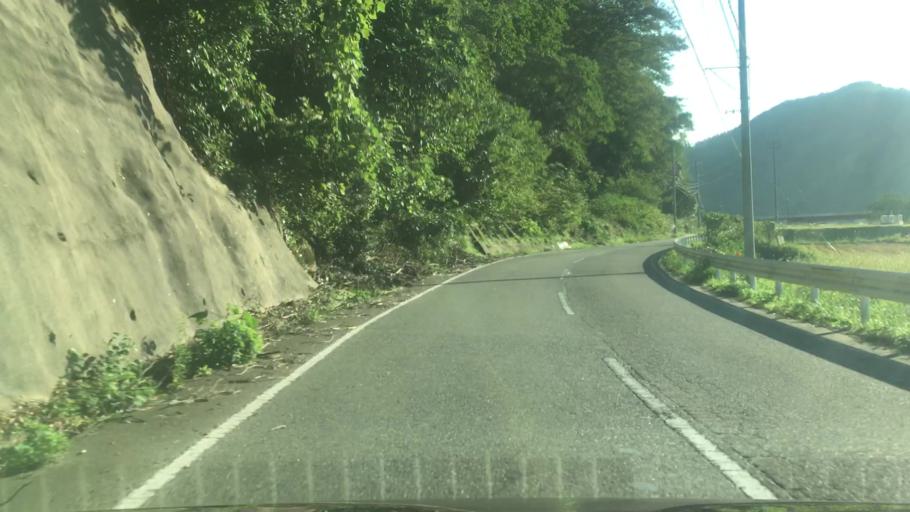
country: JP
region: Hyogo
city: Toyooka
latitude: 35.6094
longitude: 134.8085
